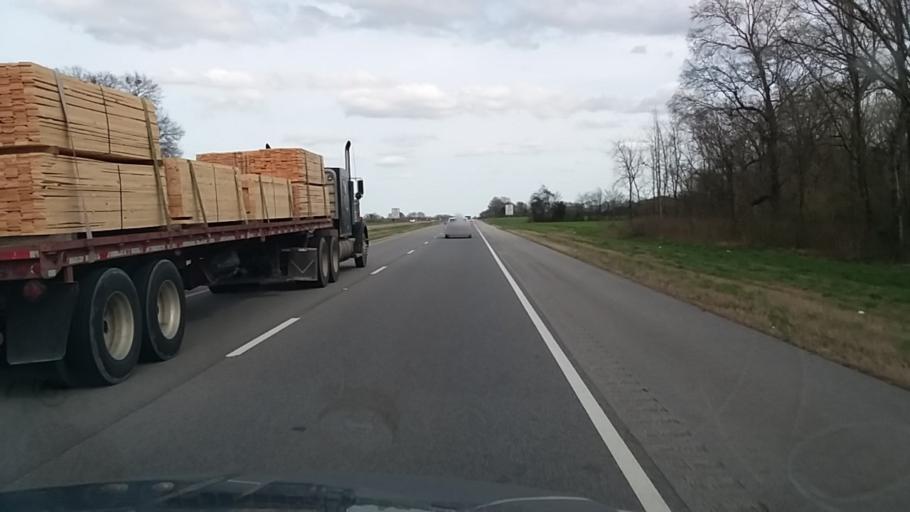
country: US
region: Alabama
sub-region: Lawrence County
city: Town Creek
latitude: 34.6841
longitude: -87.5403
